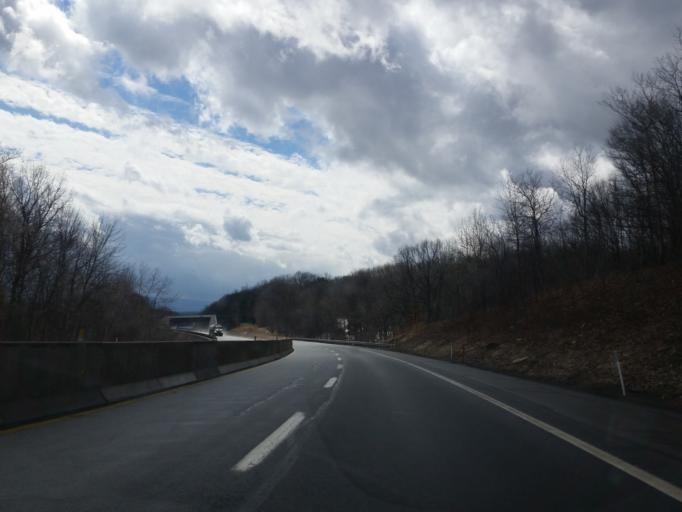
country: US
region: Pennsylvania
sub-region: Lackawanna County
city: Chinchilla
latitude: 41.4386
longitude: -75.7006
